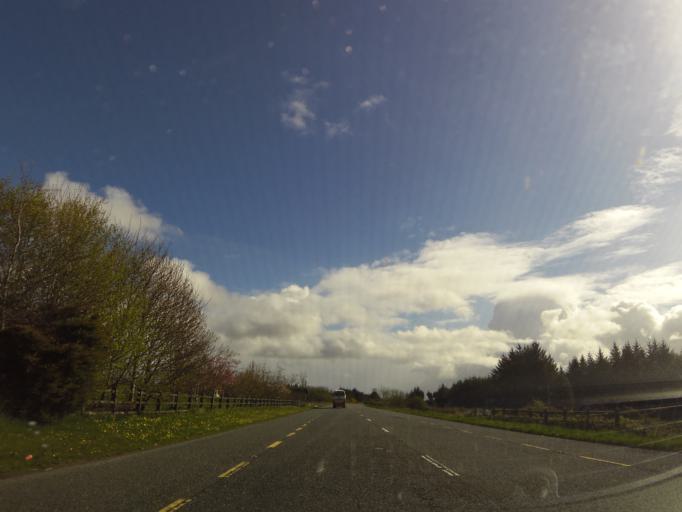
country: IE
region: Connaught
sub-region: Maigh Eo
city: Ballyhaunis
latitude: 53.8777
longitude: -8.8306
